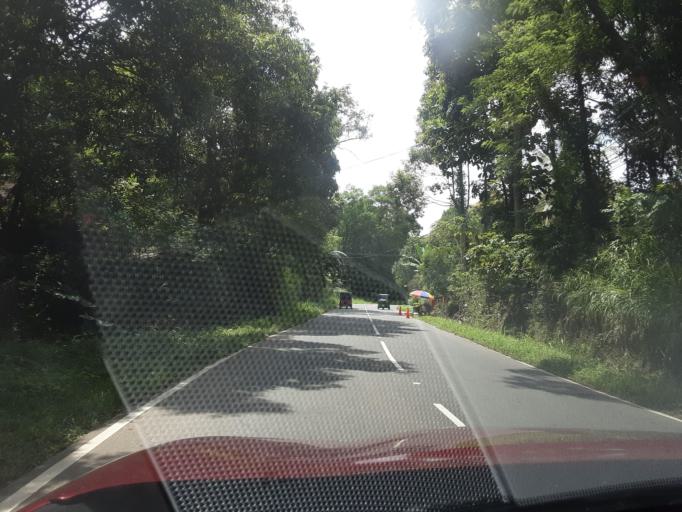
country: LK
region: Uva
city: Monaragala
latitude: 6.8949
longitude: 81.2555
